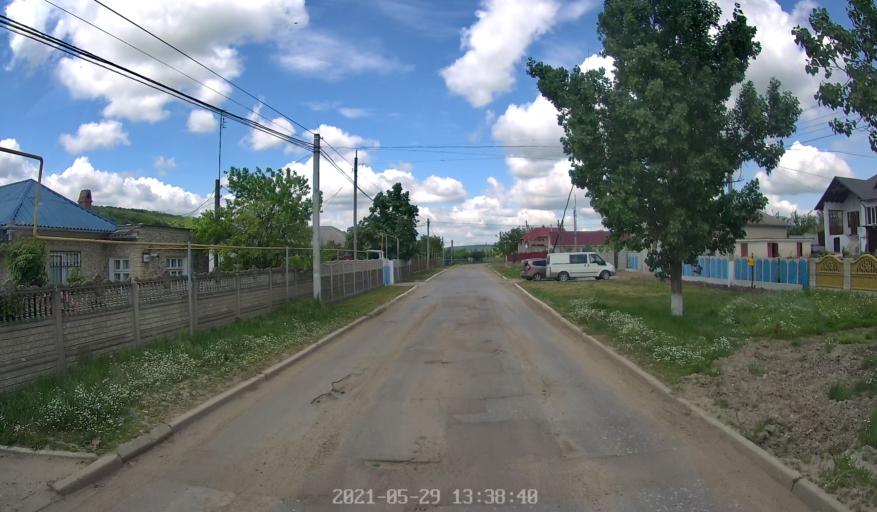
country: MD
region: Hincesti
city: Hincesti
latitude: 46.8315
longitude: 28.6762
